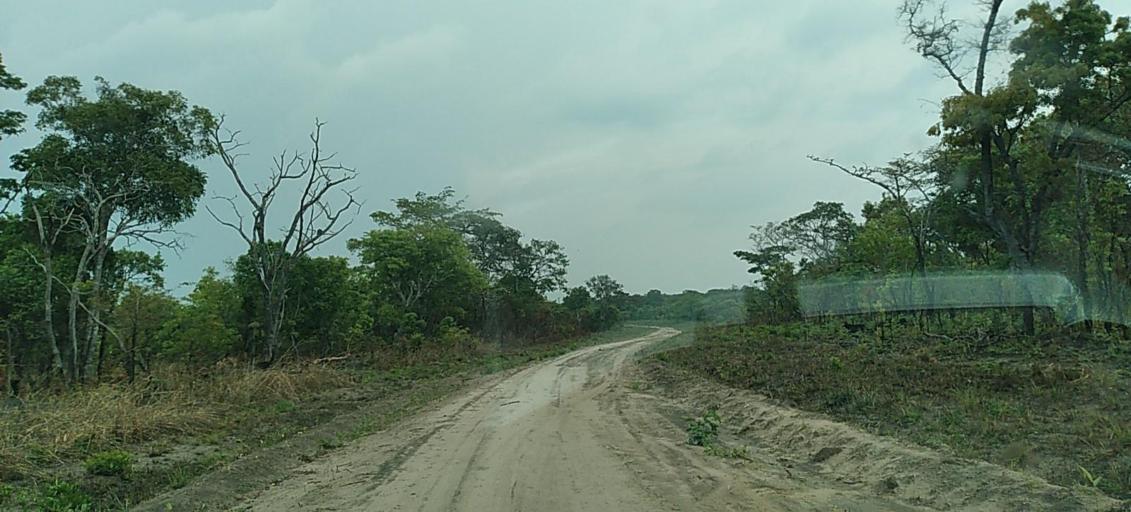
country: ZM
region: North-Western
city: Mwinilunga
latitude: -11.4260
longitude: 24.5926
